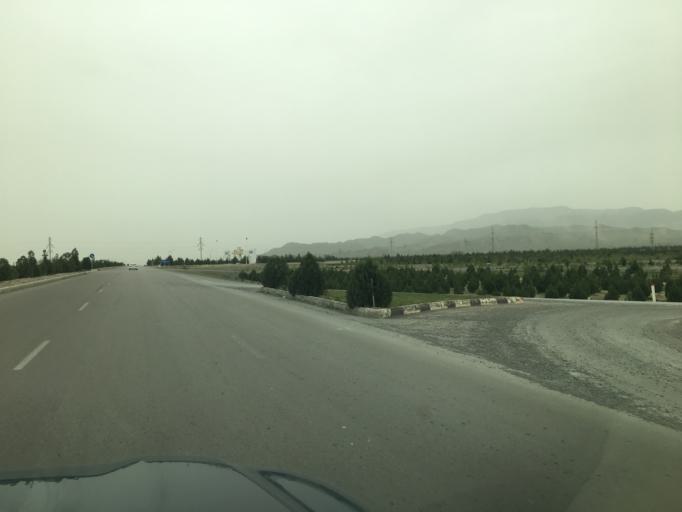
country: TM
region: Ahal
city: Baharly
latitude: 38.2850
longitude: 57.6606
